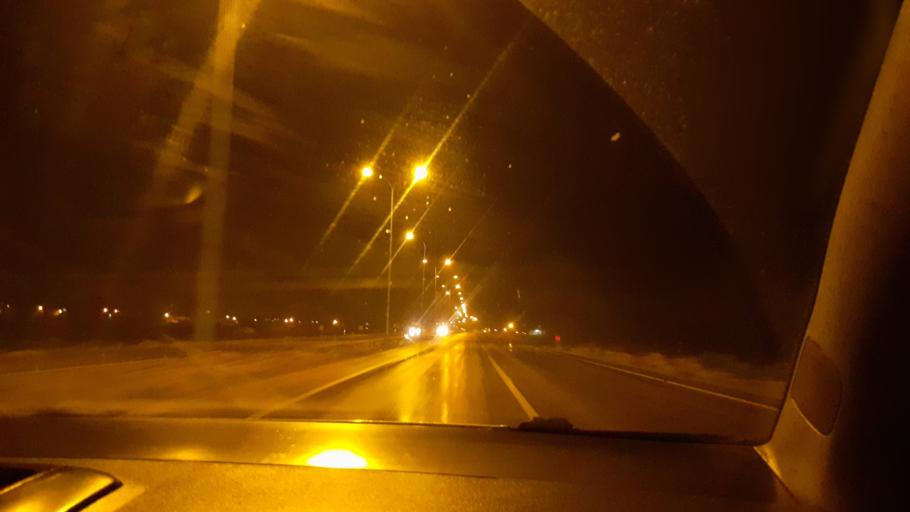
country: TR
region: Hatay
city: Aktepe
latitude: 36.7180
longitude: 36.5117
